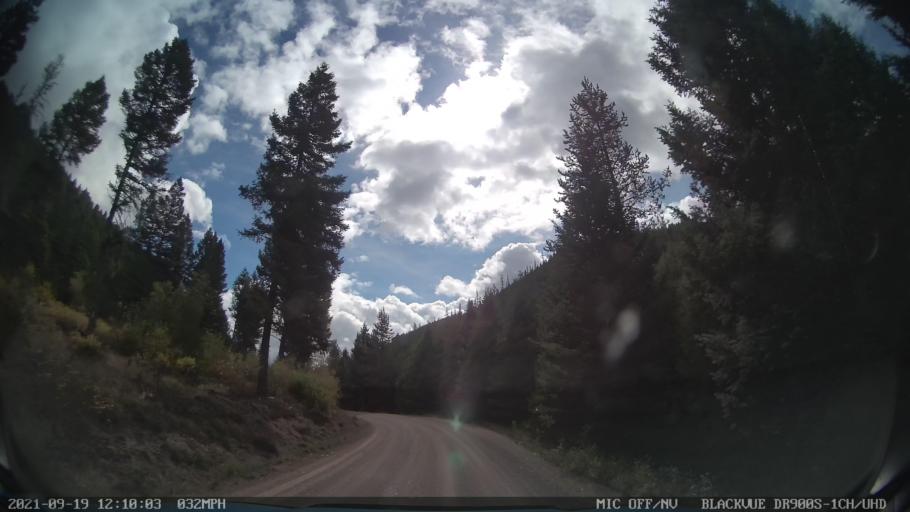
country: US
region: Montana
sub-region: Missoula County
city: Seeley Lake
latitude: 47.1807
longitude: -113.3870
